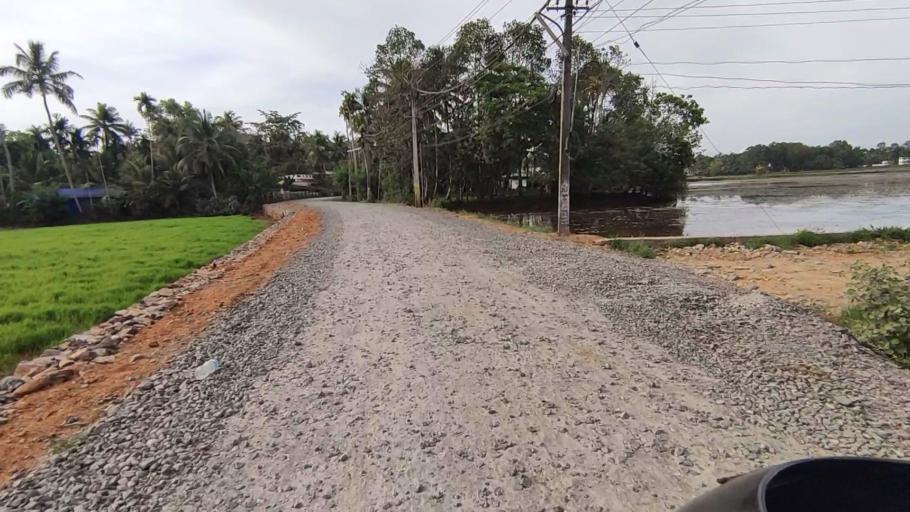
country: IN
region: Kerala
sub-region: Kottayam
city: Kottayam
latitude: 9.5784
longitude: 76.4919
